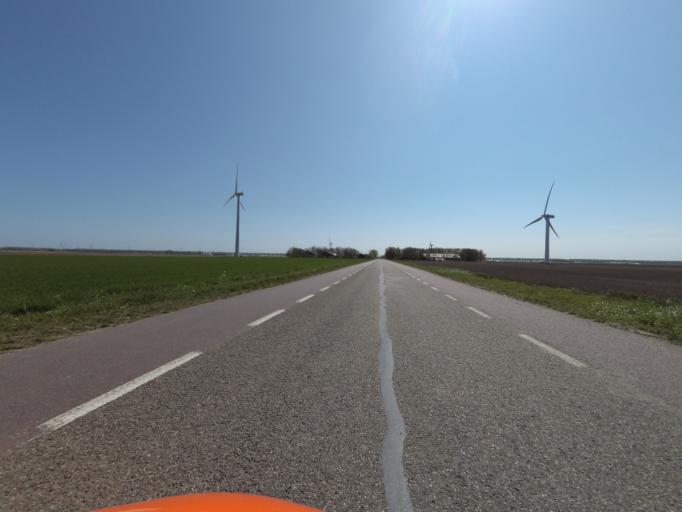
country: NL
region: Flevoland
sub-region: Gemeente Lelystad
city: Lelystad
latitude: 52.4036
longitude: 5.4230
